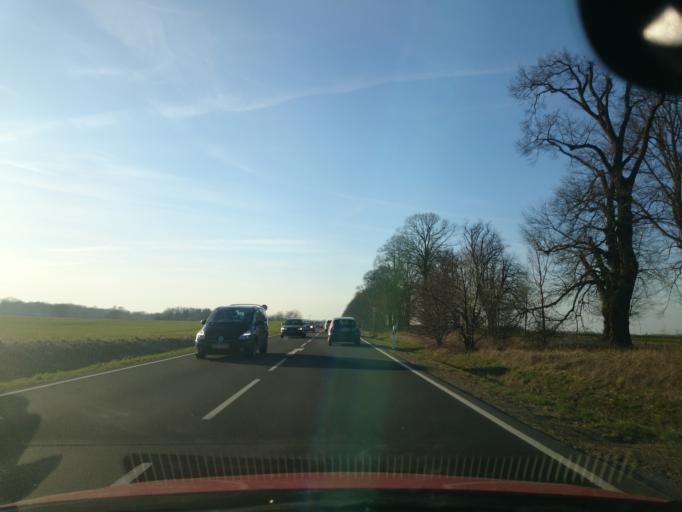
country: DE
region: Mecklenburg-Vorpommern
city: Brandshagen
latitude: 54.2271
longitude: 13.2119
